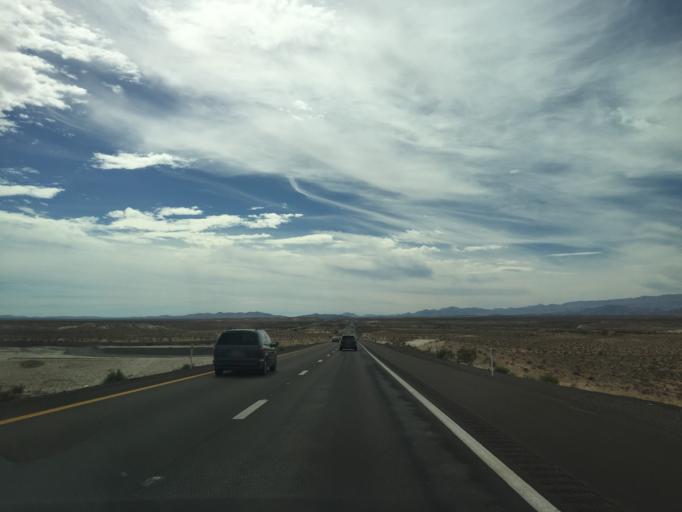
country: US
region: Nevada
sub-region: Clark County
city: Moapa Town
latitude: 36.5695
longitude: -114.6729
